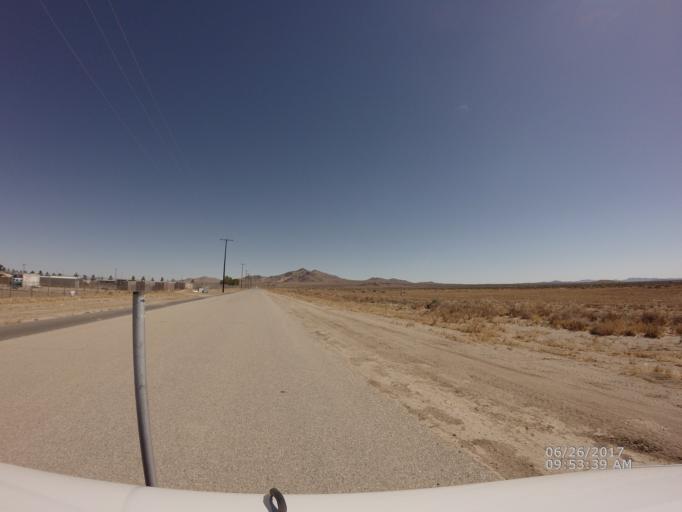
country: US
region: California
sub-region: Los Angeles County
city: Lake Los Angeles
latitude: 34.6294
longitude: -117.8093
